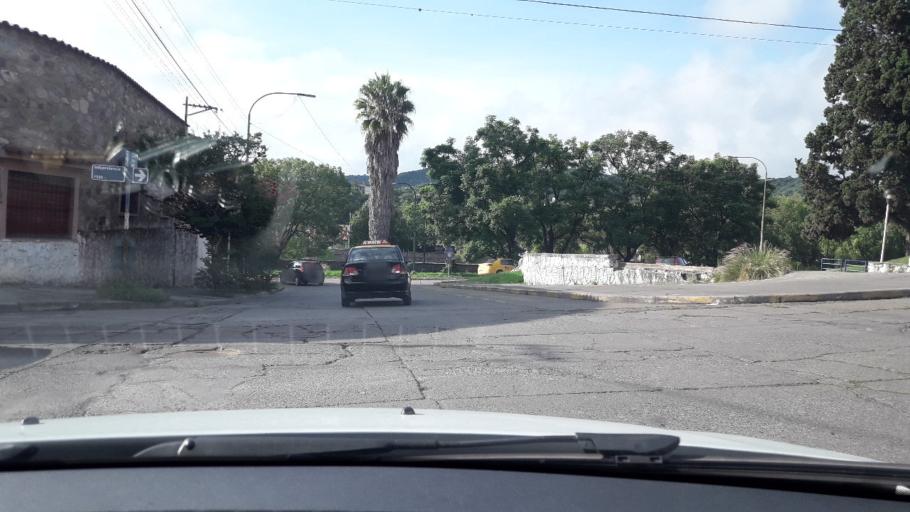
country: AR
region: Jujuy
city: San Salvador de Jujuy
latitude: -24.1885
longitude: -65.3094
